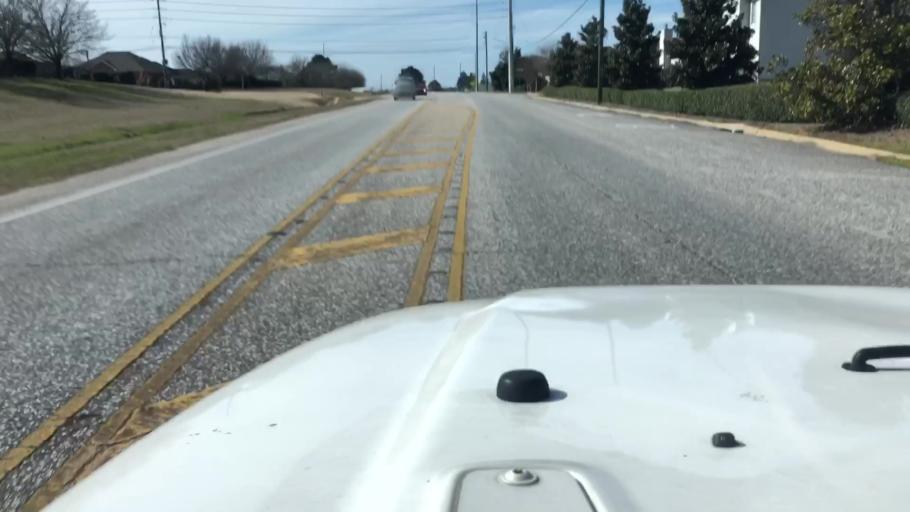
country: US
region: Alabama
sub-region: Elmore County
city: Blue Ridge
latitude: 32.3914
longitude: -86.1745
